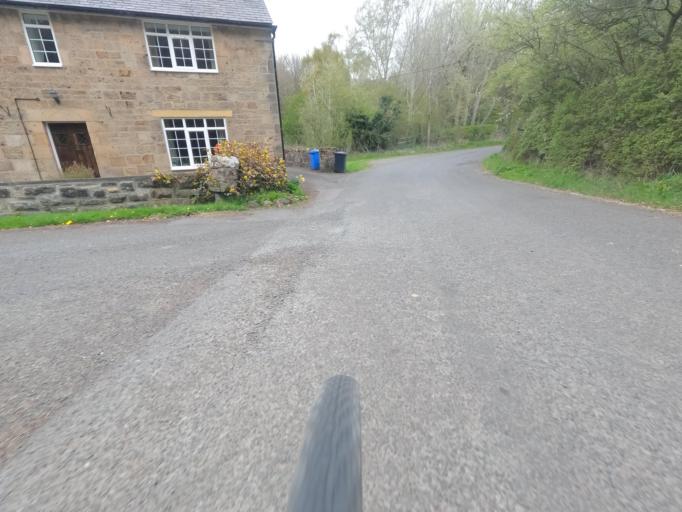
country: GB
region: England
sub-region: Northumberland
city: Meldon
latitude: 55.0727
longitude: -1.8169
